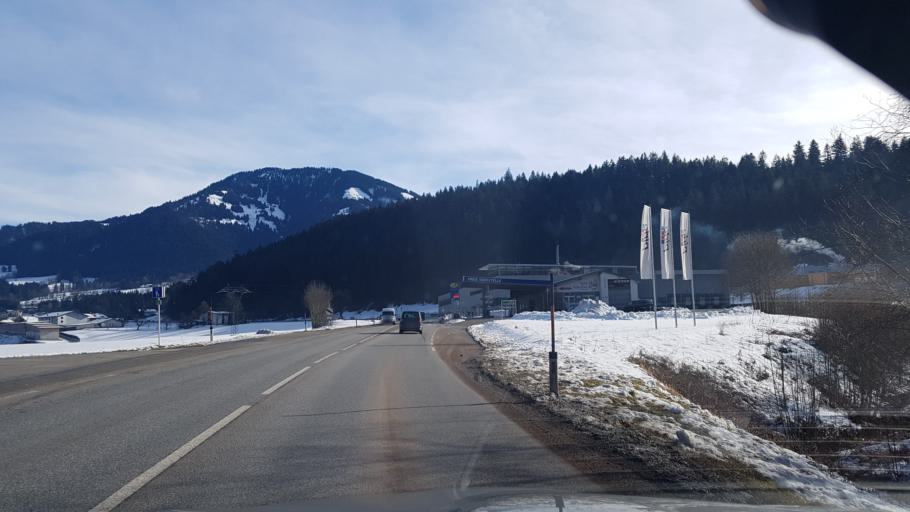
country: AT
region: Tyrol
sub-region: Politischer Bezirk Kufstein
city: Soll
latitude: 47.5182
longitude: 12.1962
